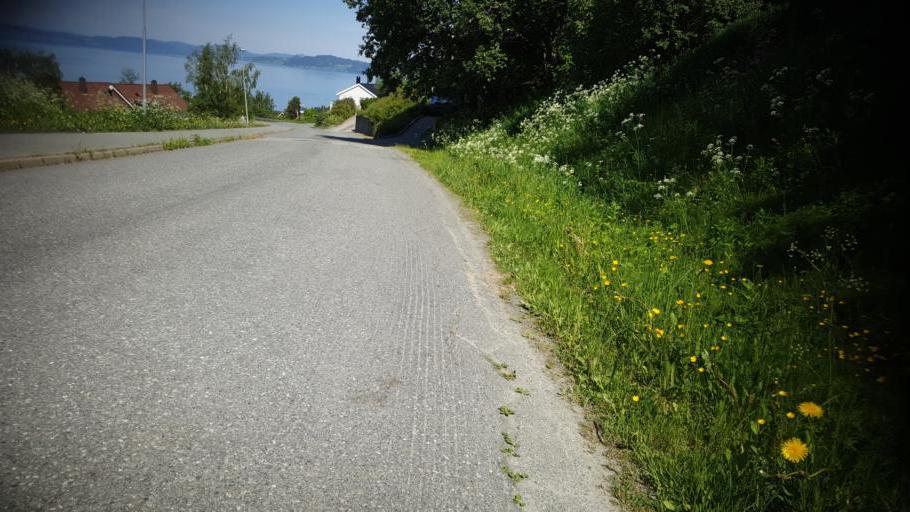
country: NO
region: Sor-Trondelag
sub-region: Malvik
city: Malvik
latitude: 63.4332
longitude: 10.6185
